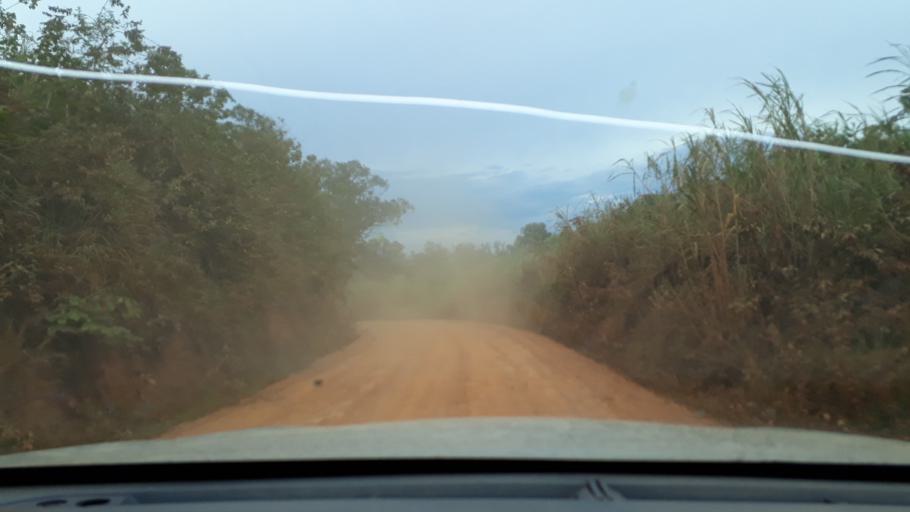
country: CD
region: Eastern Province
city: Bunia
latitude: 1.8361
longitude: 30.4571
